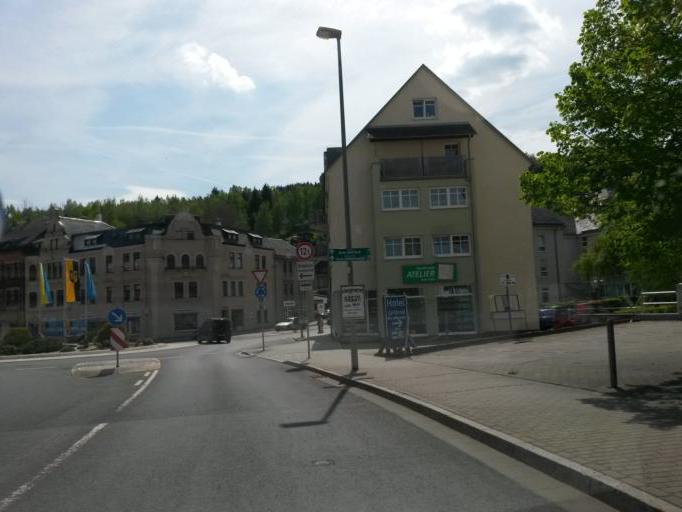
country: DE
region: Saxony
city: Klingenthal
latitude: 50.3556
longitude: 12.4683
